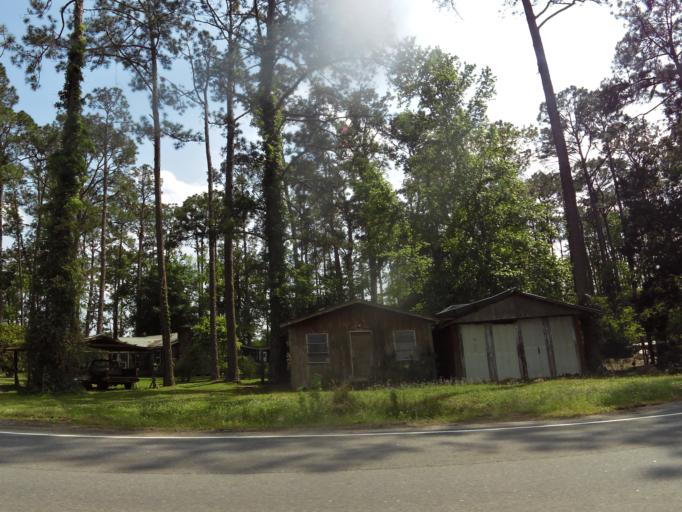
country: US
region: Georgia
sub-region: Camden County
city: Kingsland
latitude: 30.8090
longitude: -81.8033
